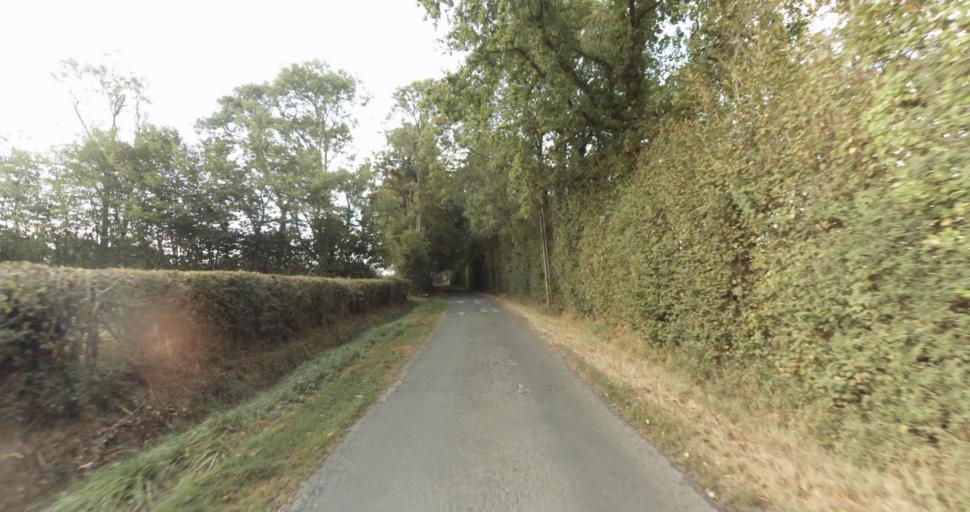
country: FR
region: Lower Normandy
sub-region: Departement de l'Orne
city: Vimoutiers
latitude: 48.9486
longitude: 0.2403
